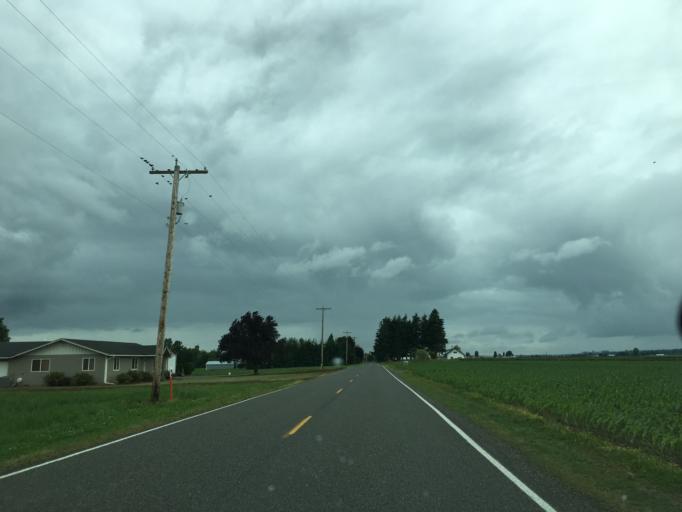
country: US
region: Washington
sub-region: Whatcom County
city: Everson
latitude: 48.9821
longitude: -122.3747
